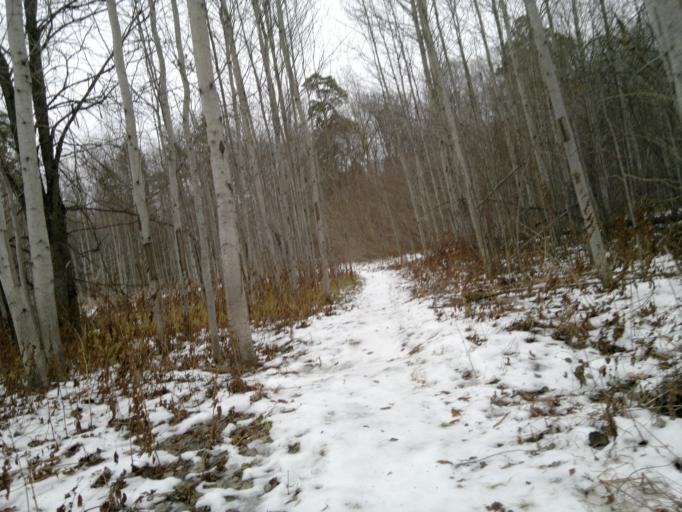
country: RU
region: Mariy-El
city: Yoshkar-Ola
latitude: 56.6122
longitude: 47.9341
